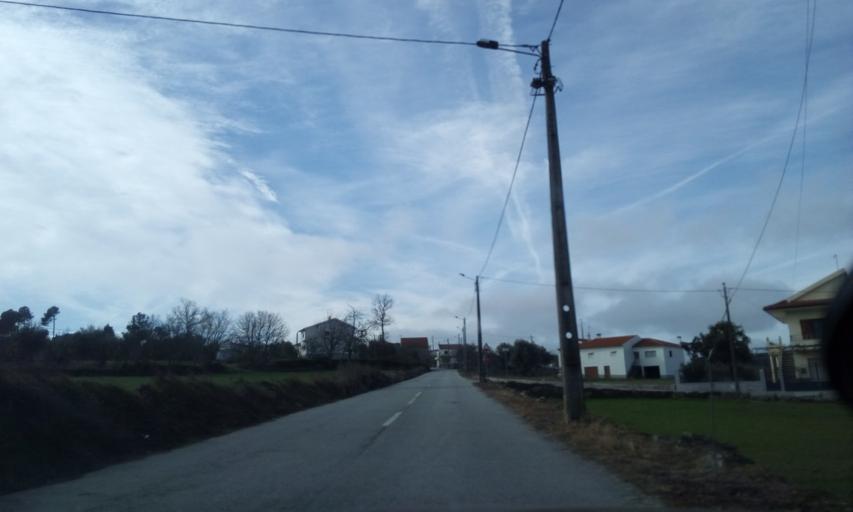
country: PT
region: Guarda
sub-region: Fornos de Algodres
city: Fornos de Algodres
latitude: 40.6593
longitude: -7.5329
